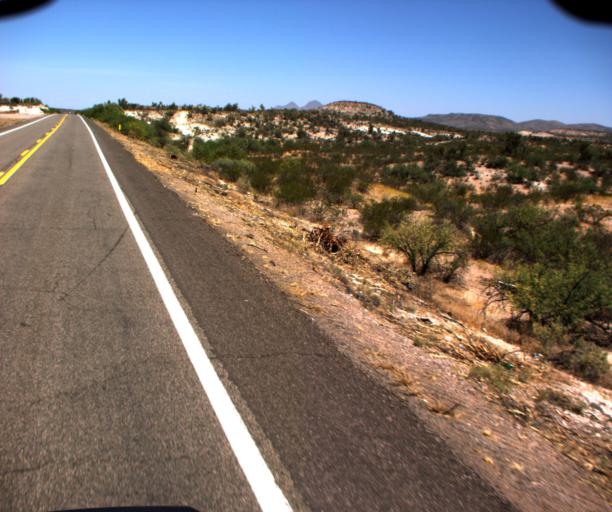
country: US
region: Arizona
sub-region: Graham County
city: Bylas
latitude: 33.2357
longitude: -110.2475
